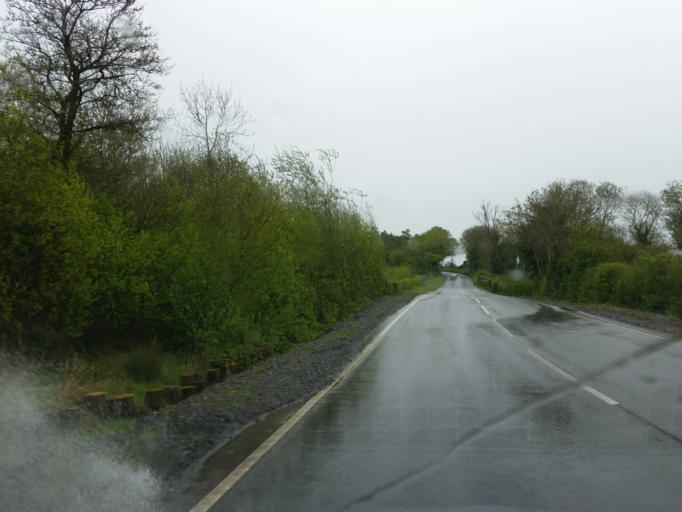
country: GB
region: Northern Ireland
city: Lisnaskea
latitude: 54.2134
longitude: -7.4721
